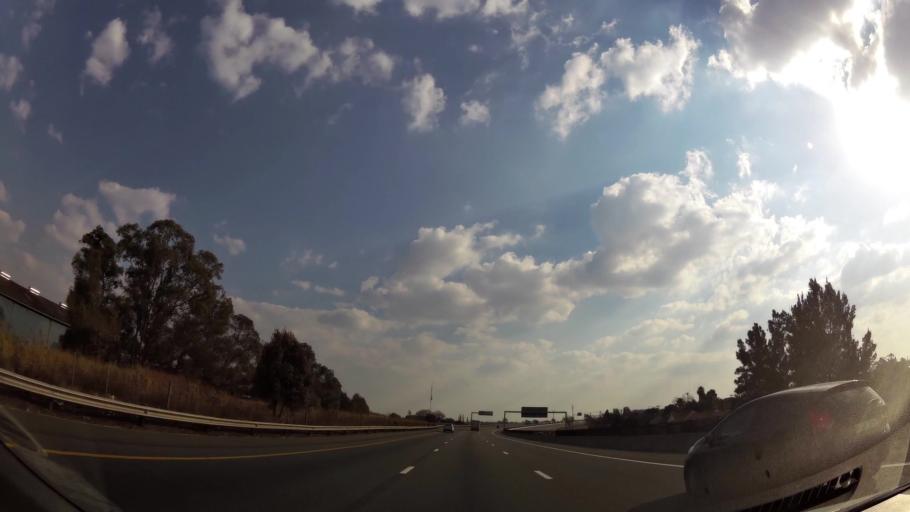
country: ZA
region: Gauteng
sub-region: Ekurhuleni Metropolitan Municipality
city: Germiston
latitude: -26.2575
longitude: 28.1802
